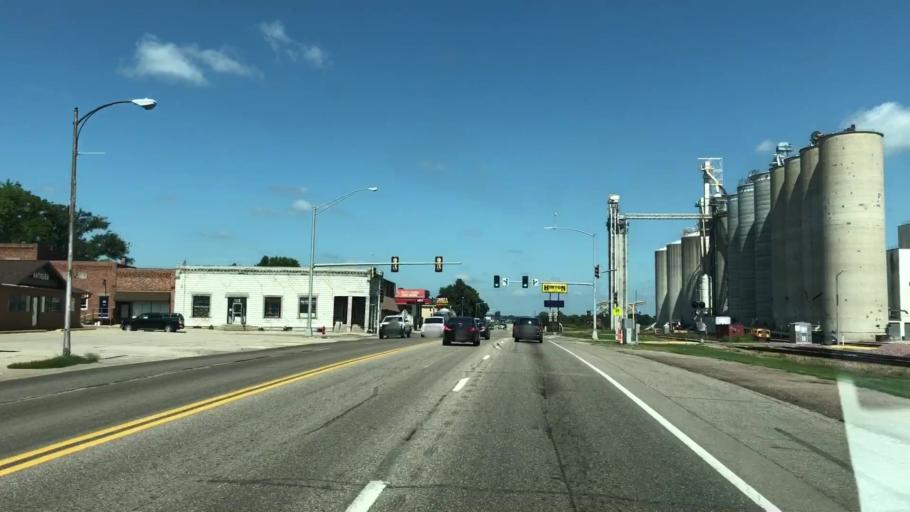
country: US
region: Iowa
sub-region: Woodbury County
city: Sioux City
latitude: 42.6259
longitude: -96.2921
